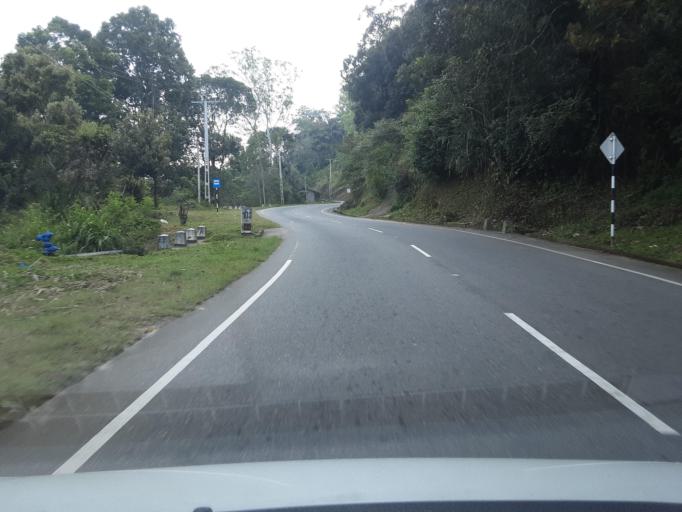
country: LK
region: Uva
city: Badulla
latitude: 6.9278
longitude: 80.9697
